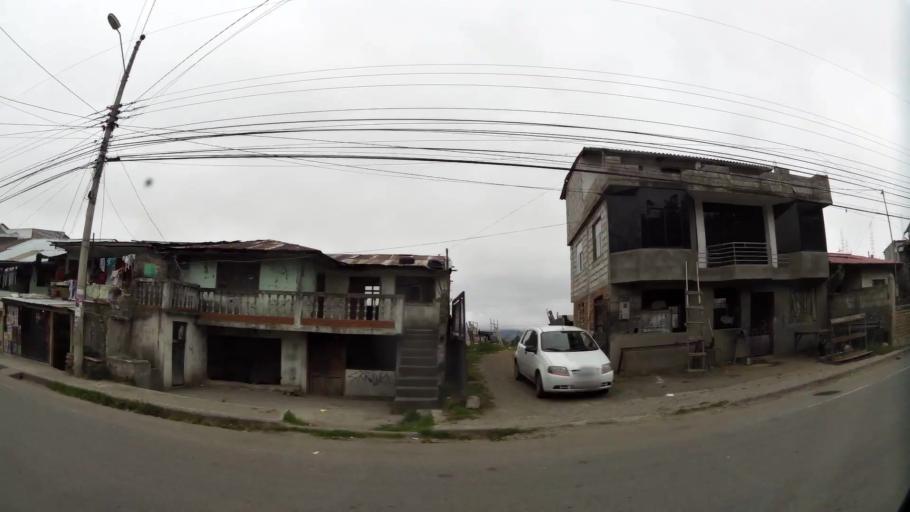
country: EC
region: Canar
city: Canar
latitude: -2.5028
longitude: -78.9287
